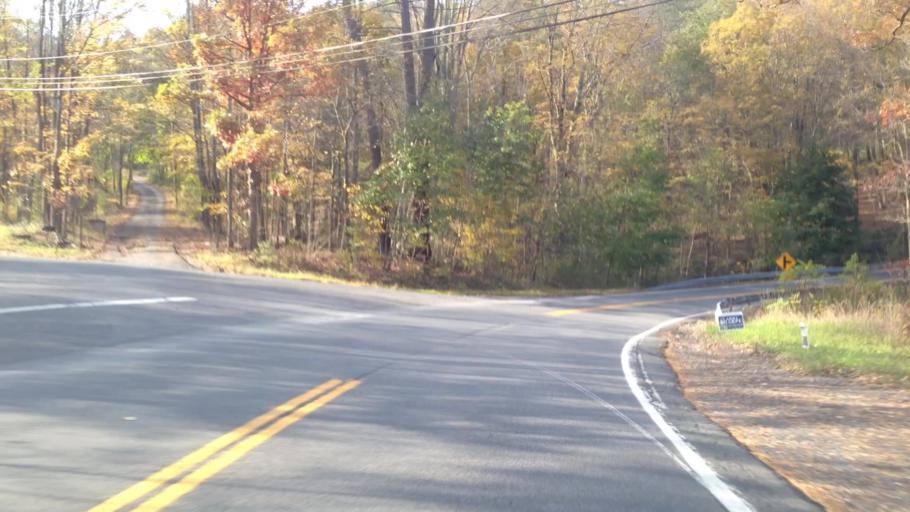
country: US
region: New York
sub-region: Ulster County
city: Tillson
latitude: 41.8211
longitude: -74.0458
